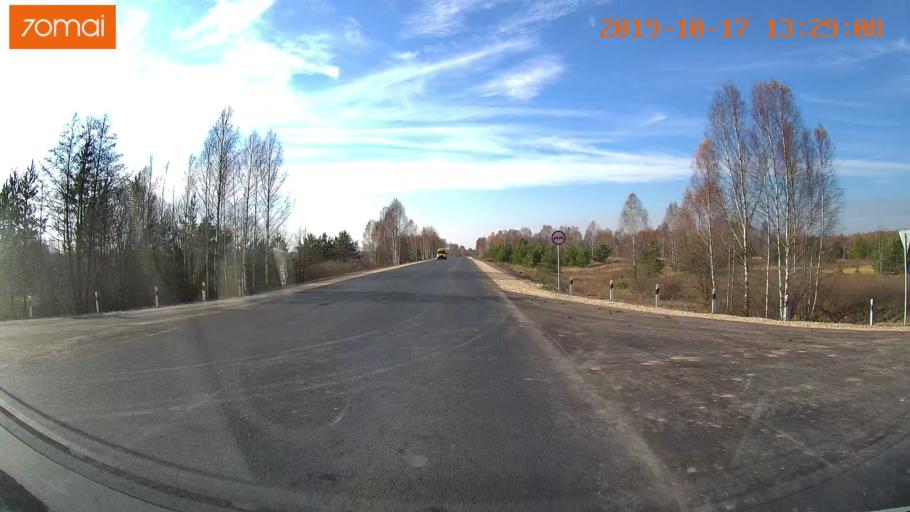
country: RU
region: Vladimir
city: Velikodvorskiy
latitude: 55.1184
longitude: 40.8490
